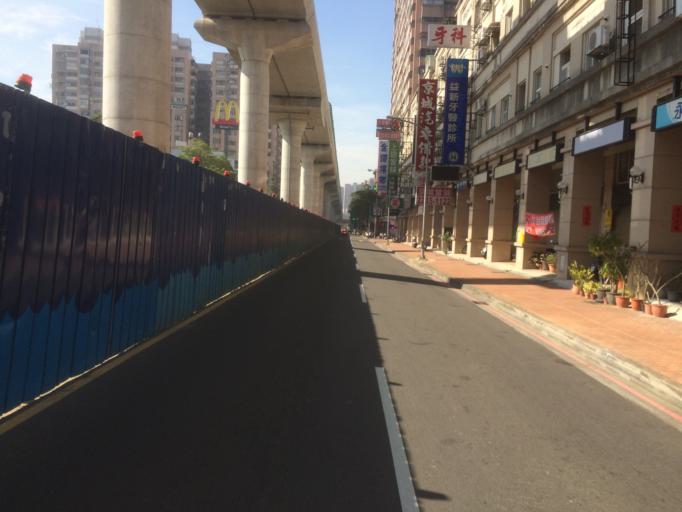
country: TW
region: Taiwan
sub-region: Taichung City
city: Taichung
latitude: 24.1805
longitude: 120.7012
